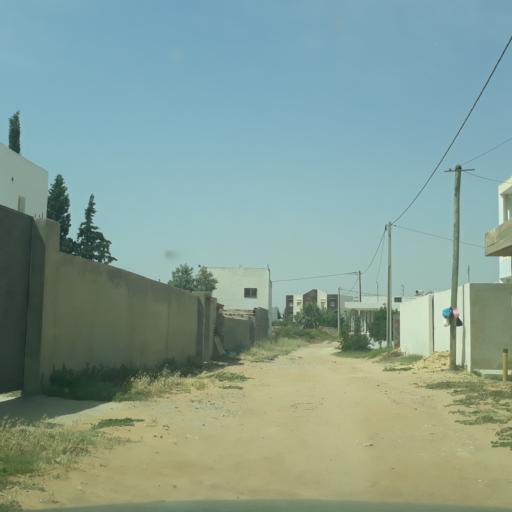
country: TN
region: Safaqis
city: Al Qarmadah
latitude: 34.7955
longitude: 10.7623
